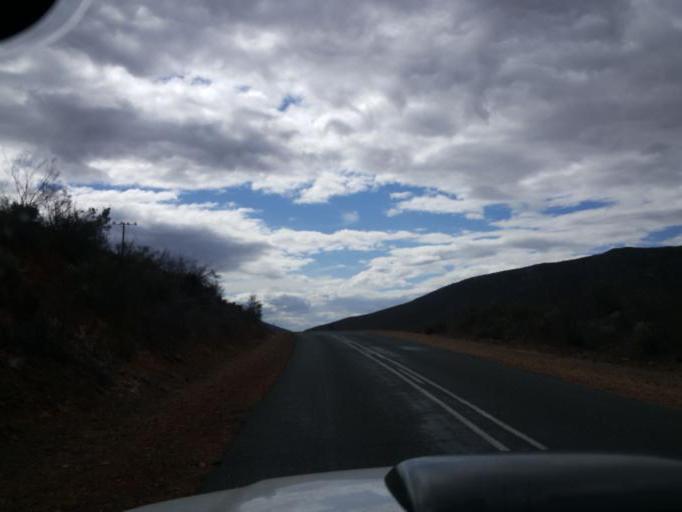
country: ZA
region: Western Cape
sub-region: Eden District Municipality
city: George
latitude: -33.8213
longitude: 22.3806
